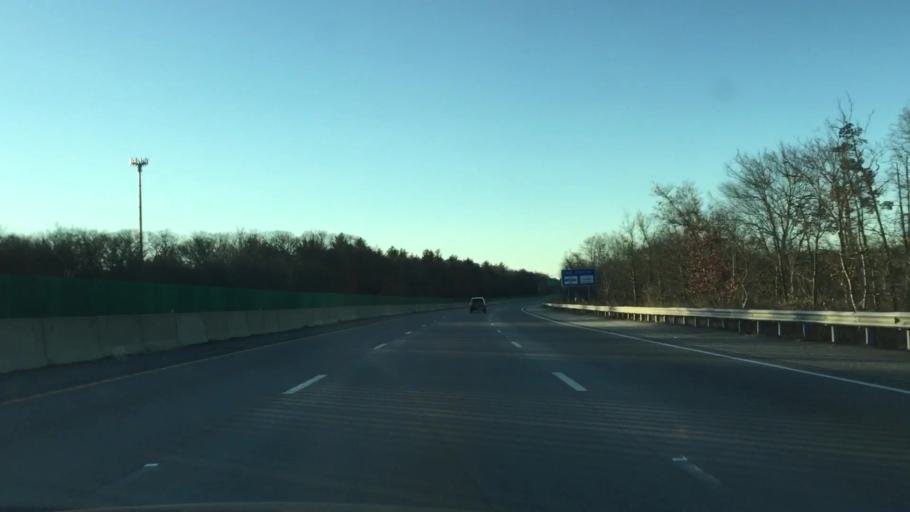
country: US
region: Massachusetts
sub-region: Plymouth County
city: West Bridgewater
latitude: 41.9819
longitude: -71.0254
